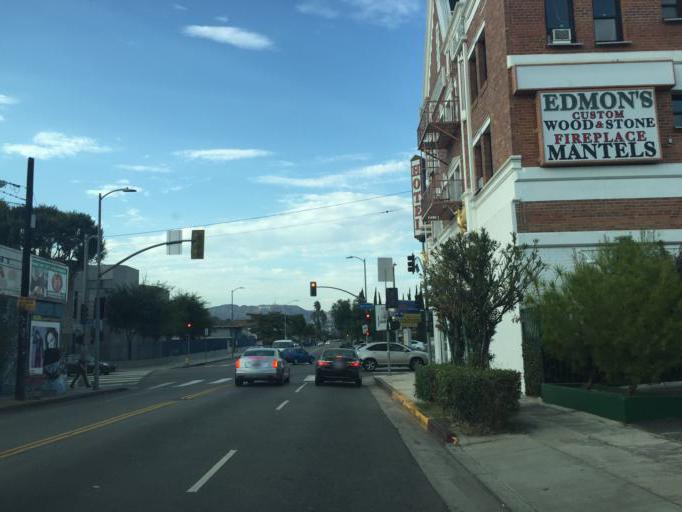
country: US
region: California
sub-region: Los Angeles County
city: Hollywood
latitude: 34.0831
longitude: -118.3135
